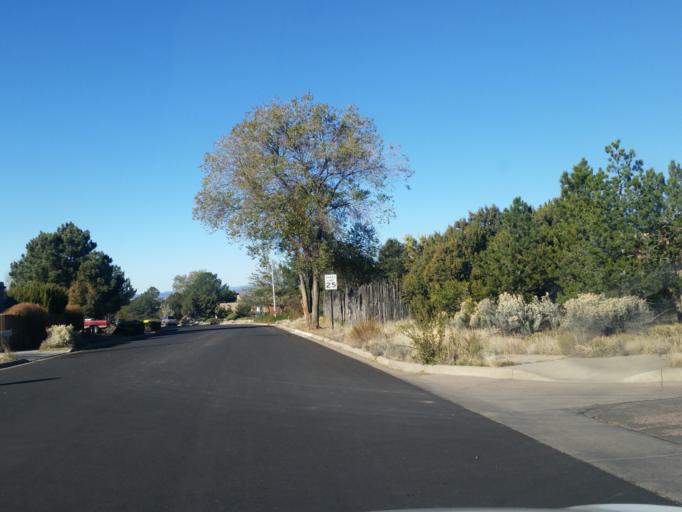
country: US
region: New Mexico
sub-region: Santa Fe County
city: Santa Fe
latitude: 35.6486
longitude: -105.9292
